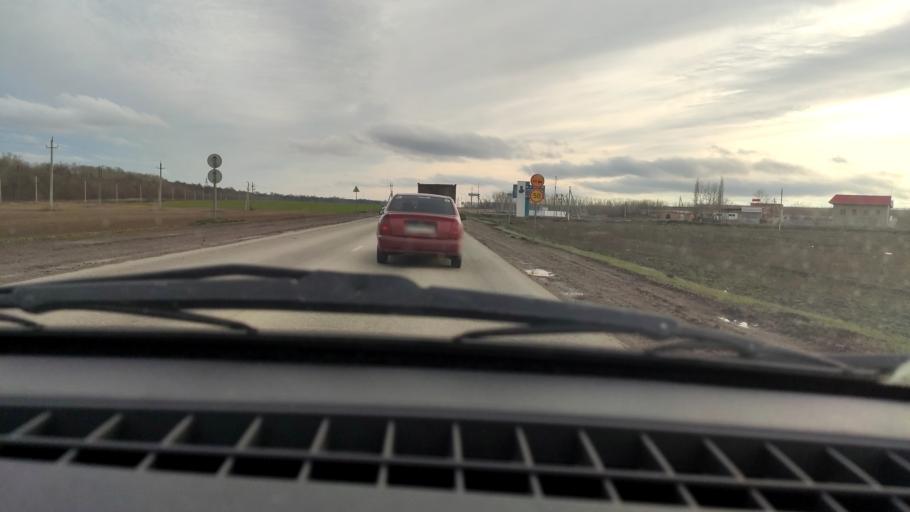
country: RU
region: Bashkortostan
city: Chishmy
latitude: 54.5691
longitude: 55.3529
